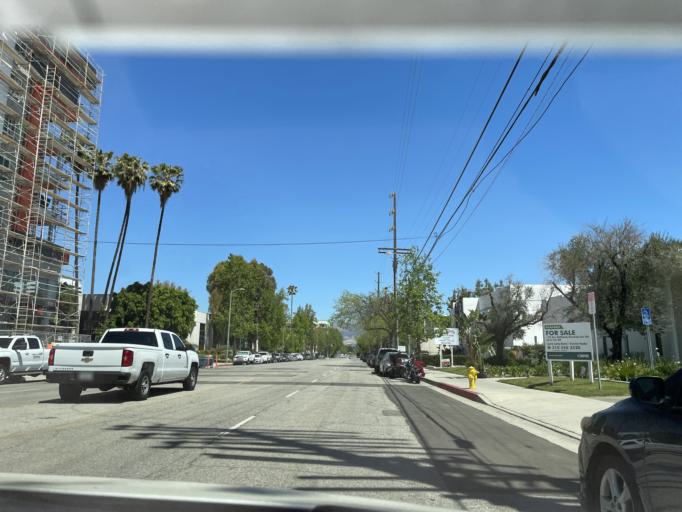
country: US
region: California
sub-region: Los Angeles County
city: Woodland Hills
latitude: 34.1803
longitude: -118.5927
